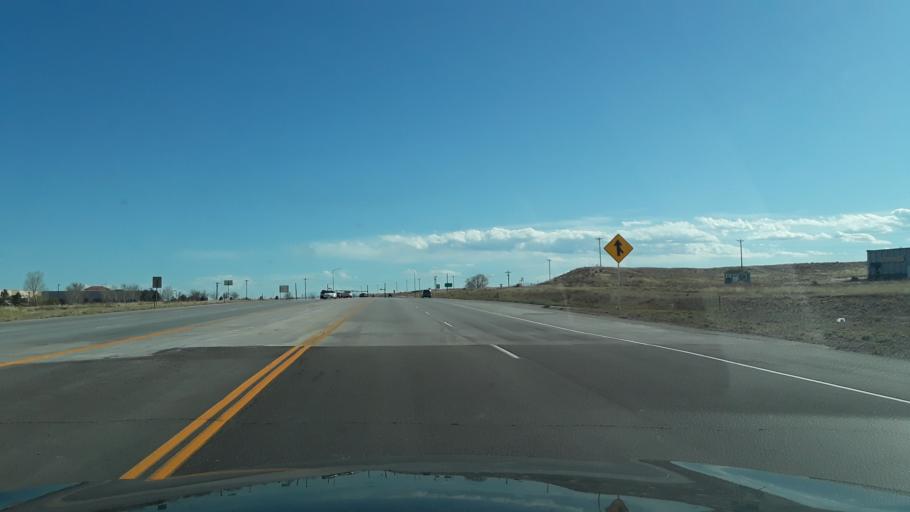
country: US
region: Colorado
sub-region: Pueblo County
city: Pueblo West
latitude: 38.3134
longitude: -104.6616
